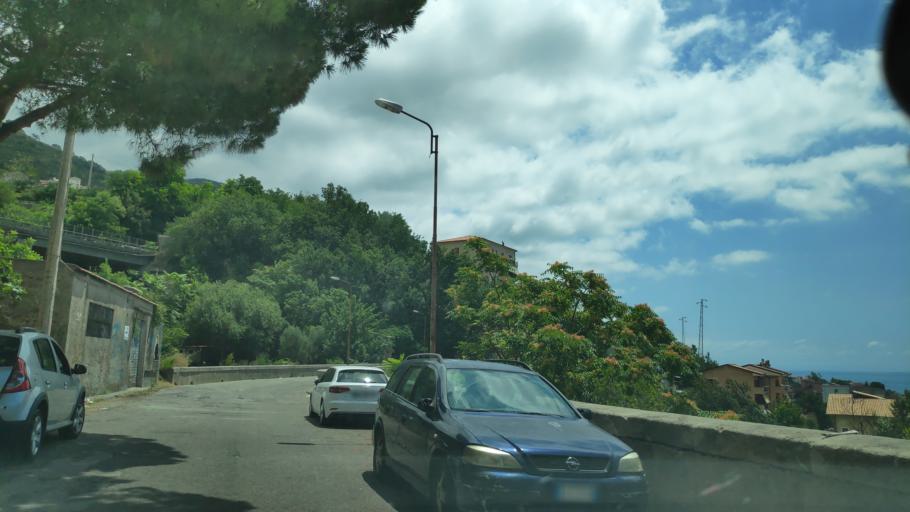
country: IT
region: Calabria
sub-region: Provincia di Cosenza
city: Paola
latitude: 39.3588
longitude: 16.0440
